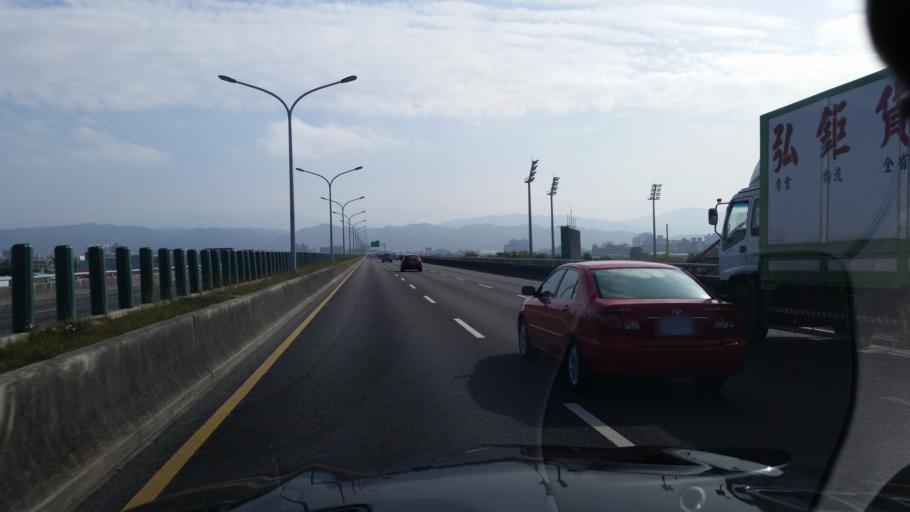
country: TW
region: Taiwan
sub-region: Taichung City
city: Taichung
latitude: 24.2010
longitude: 120.6830
